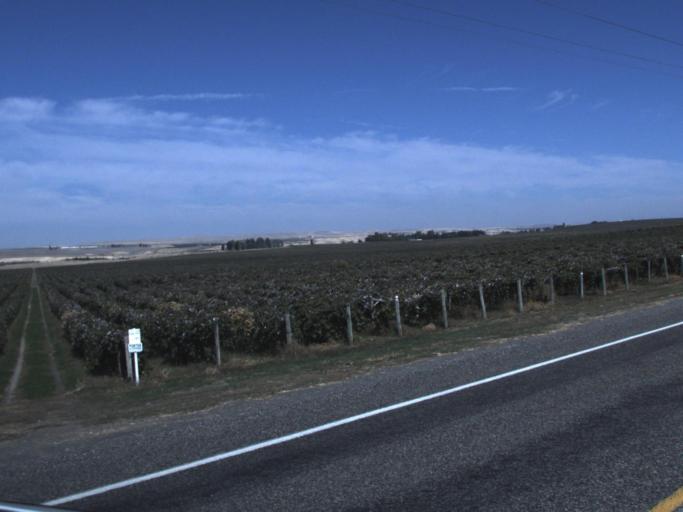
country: US
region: Washington
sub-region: Walla Walla County
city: Burbank
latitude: 46.2235
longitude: -118.8609
